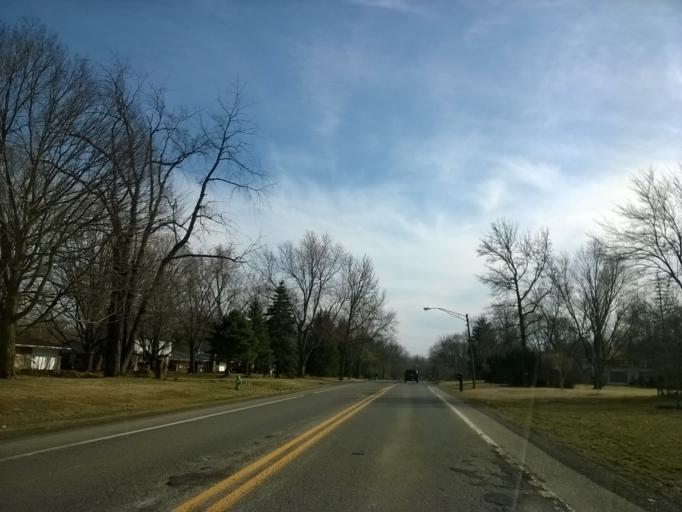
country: US
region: Indiana
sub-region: Marion County
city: Speedway
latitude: 39.8435
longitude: -86.2118
